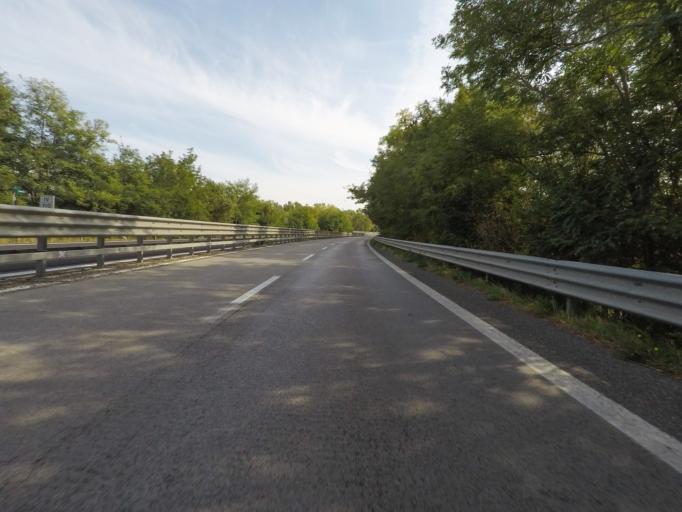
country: IT
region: Latium
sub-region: Provincia di Viterbo
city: Montalto di Castro
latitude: 42.3536
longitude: 11.5967
